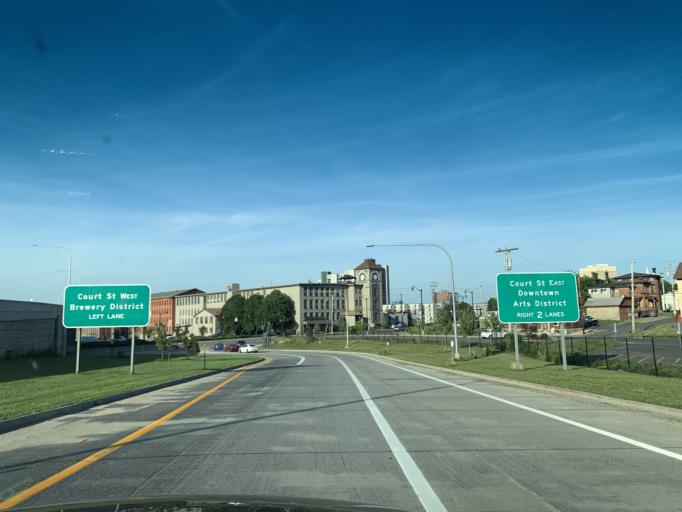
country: US
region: New York
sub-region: Oneida County
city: Utica
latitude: 43.1009
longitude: -75.2419
